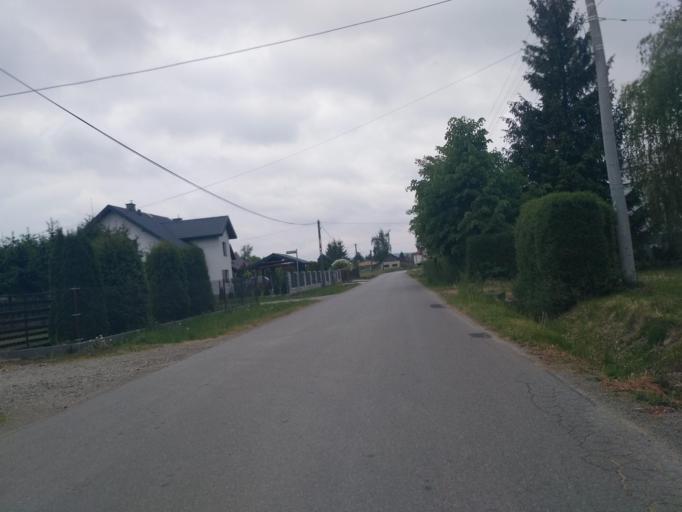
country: PL
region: Subcarpathian Voivodeship
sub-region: Krosno
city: Krosno
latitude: 49.6700
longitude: 21.7259
